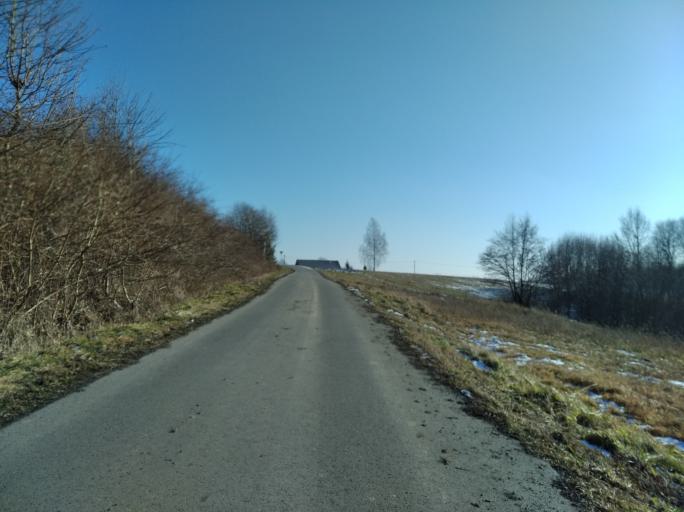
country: PL
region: Subcarpathian Voivodeship
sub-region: Powiat strzyzowski
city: Konieczkowa
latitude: 49.8591
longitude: 21.9565
